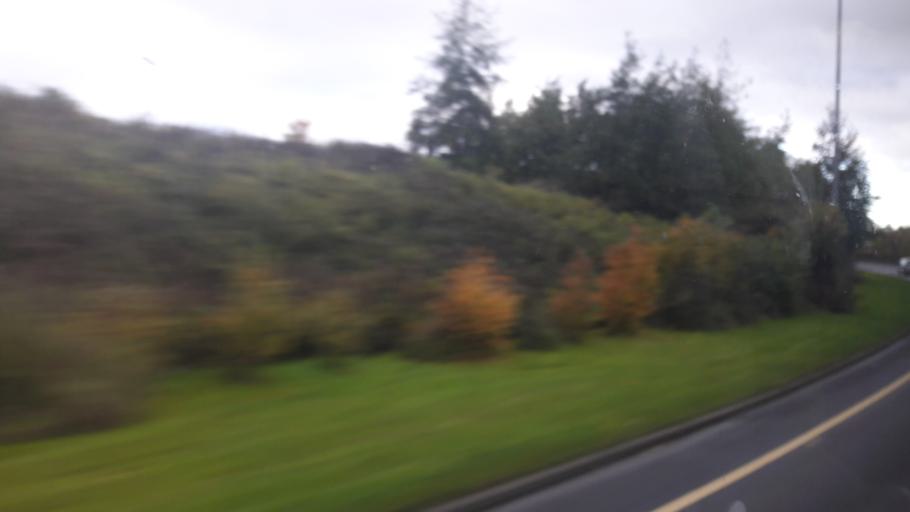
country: IE
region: Leinster
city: Kinsealy-Drinan
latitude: 53.4266
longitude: -6.2193
